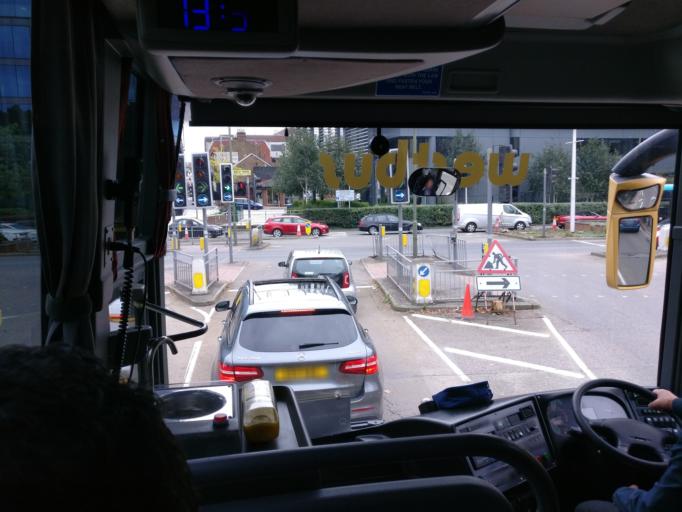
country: GB
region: England
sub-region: Surrey
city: Woking
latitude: 51.3217
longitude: -0.5581
